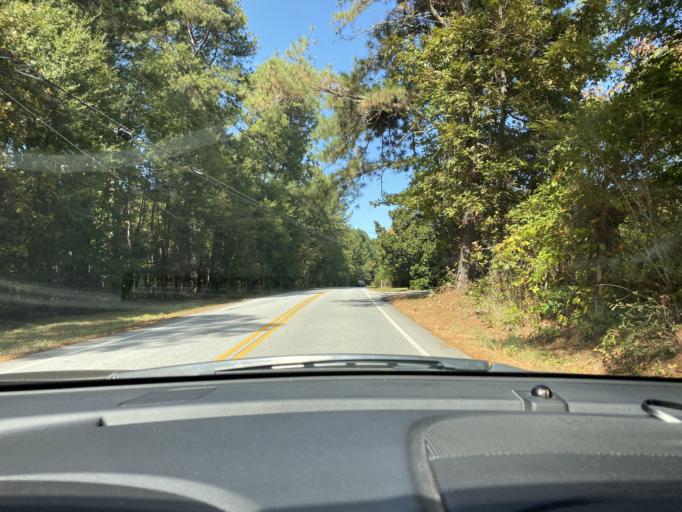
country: US
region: Georgia
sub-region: Walton County
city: Loganville
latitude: 33.8709
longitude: -83.9102
